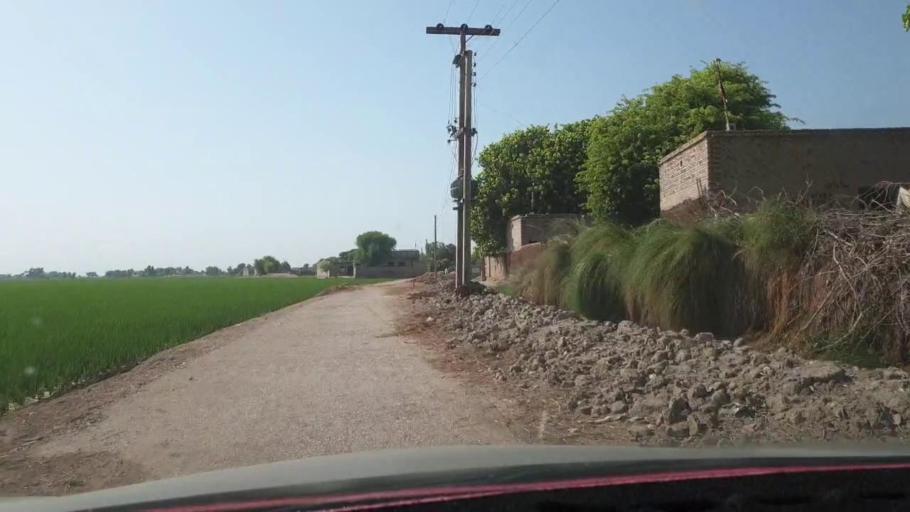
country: PK
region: Sindh
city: Nasirabad
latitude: 27.3817
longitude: 67.8806
